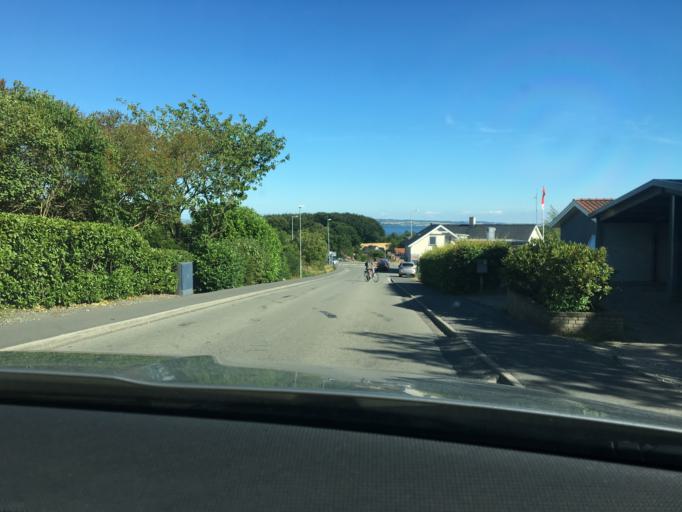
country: DK
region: Central Jutland
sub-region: Syddjurs Kommune
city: Hornslet
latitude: 56.3009
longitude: 10.3631
